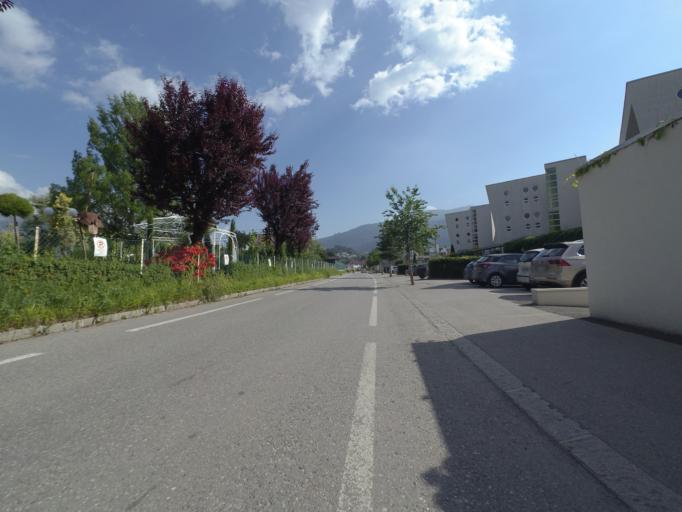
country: AT
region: Carinthia
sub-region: Politischer Bezirk Spittal an der Drau
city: Seeboden
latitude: 46.8144
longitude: 13.5099
